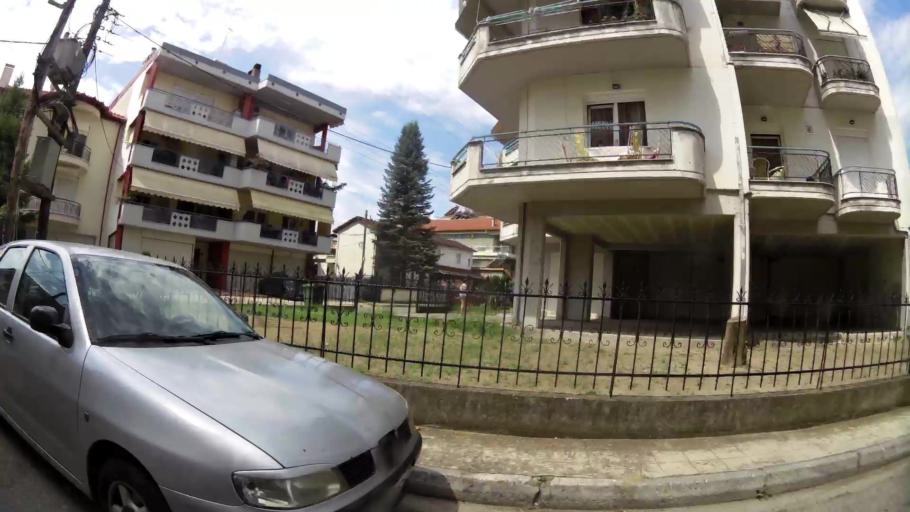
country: GR
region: Central Macedonia
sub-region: Nomos Pierias
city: Katerini
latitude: 40.2707
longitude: 22.4952
